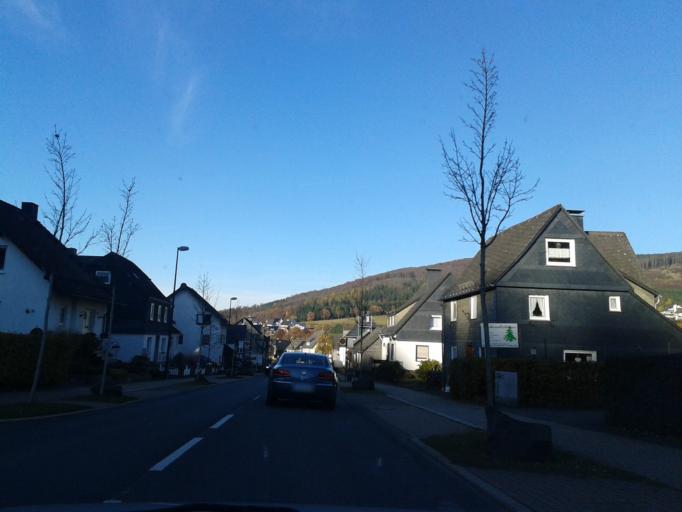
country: DE
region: North Rhine-Westphalia
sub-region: Regierungsbezirk Arnsberg
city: Winterberg
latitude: 51.2563
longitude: 8.5284
